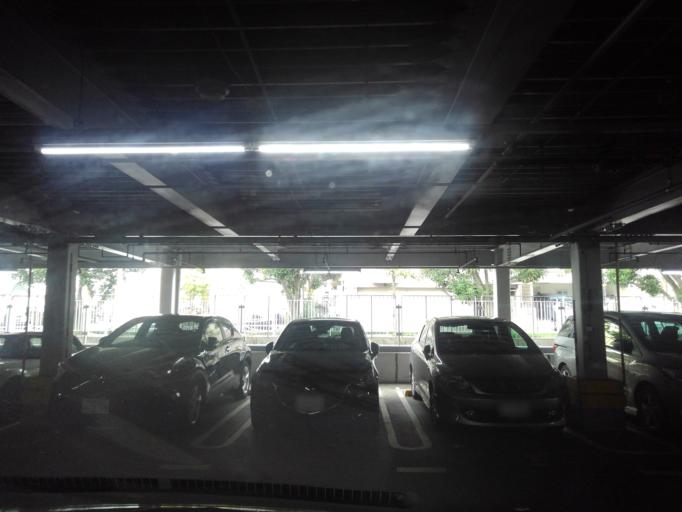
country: JP
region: Saitama
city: Tokorozawa
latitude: 35.8023
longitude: 139.4401
